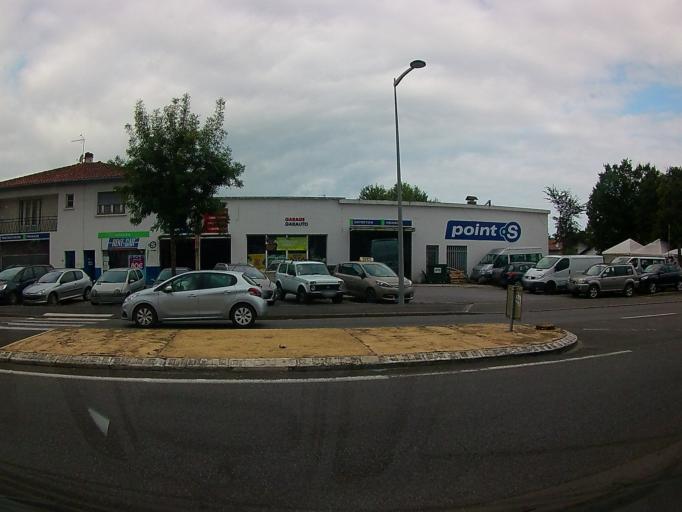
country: FR
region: Aquitaine
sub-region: Departement des Landes
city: Labenne
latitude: 43.5890
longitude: -1.4282
